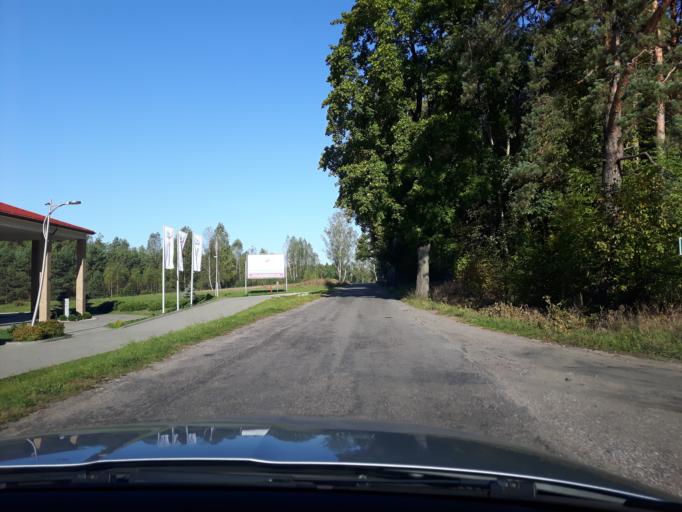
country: PL
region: Warmian-Masurian Voivodeship
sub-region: Powiat olsztynski
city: Gietrzwald
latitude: 53.7148
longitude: 20.2047
